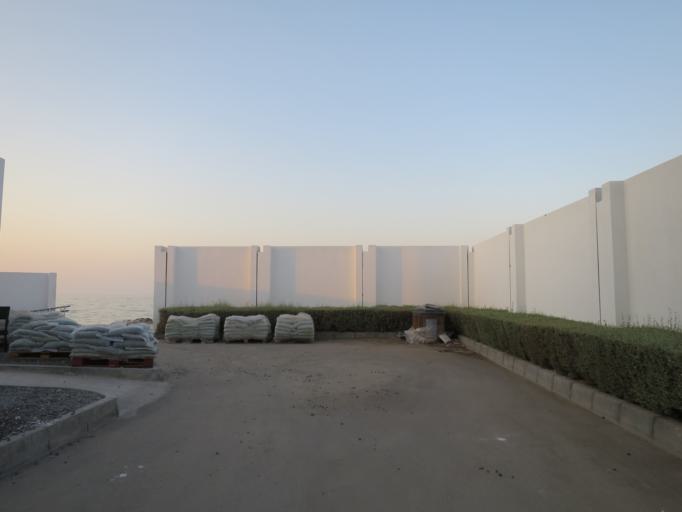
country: OM
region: Muhafazat Masqat
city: Bawshar
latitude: 23.6036
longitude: 58.4003
